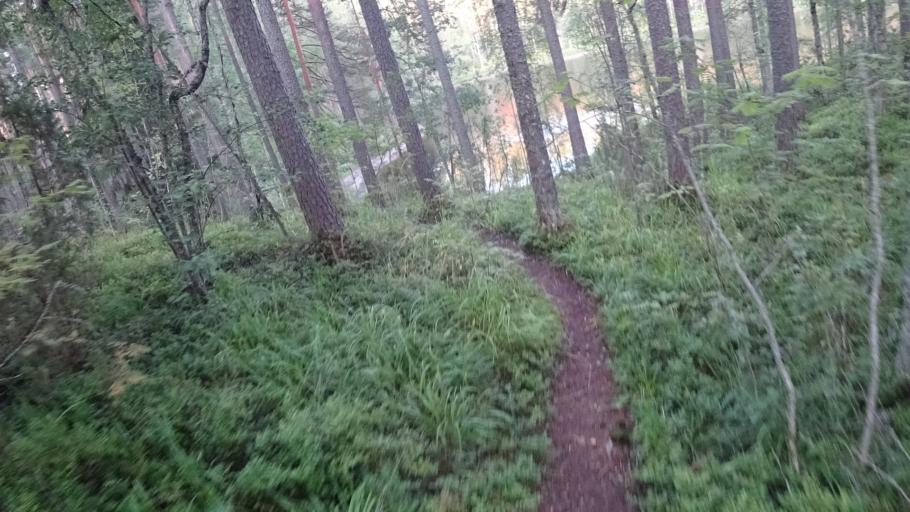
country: FI
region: North Karelia
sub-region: Joensuu
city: Ilomantsi
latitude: 62.5812
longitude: 31.1677
